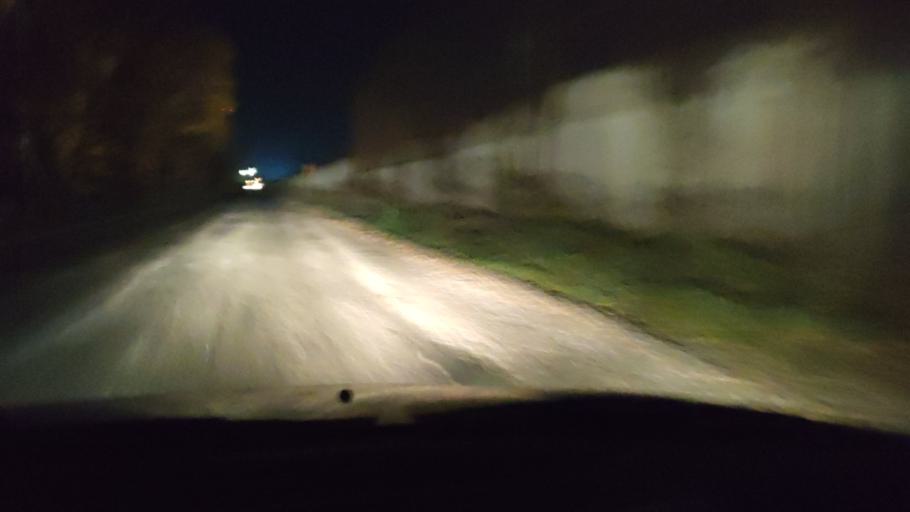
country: RU
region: Perm
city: Overyata
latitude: 58.0269
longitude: 55.9207
